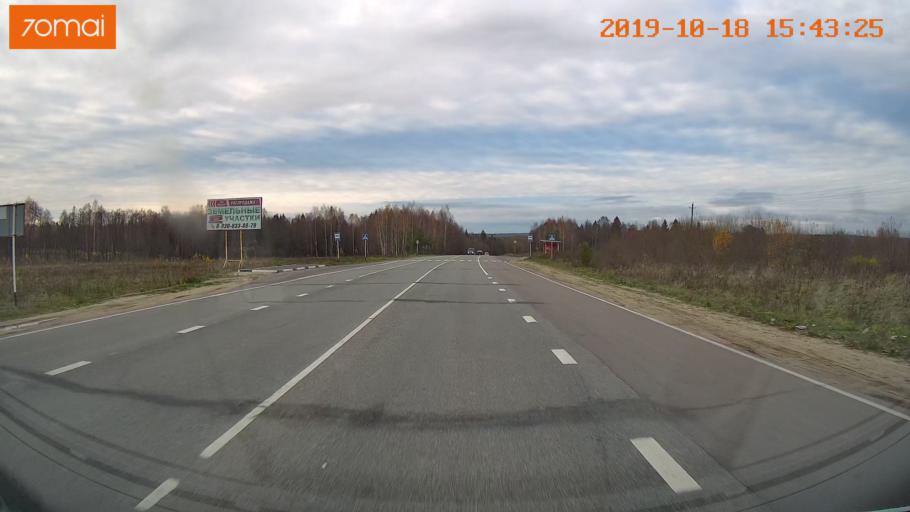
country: RU
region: Vladimir
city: Golovino
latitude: 55.9674
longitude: 40.5512
